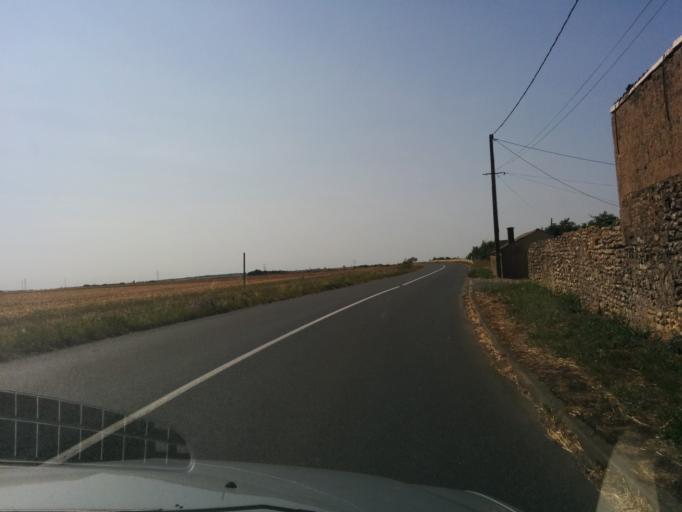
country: FR
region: Poitou-Charentes
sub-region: Departement de la Vienne
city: Moncontour
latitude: 46.8105
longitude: -0.0393
